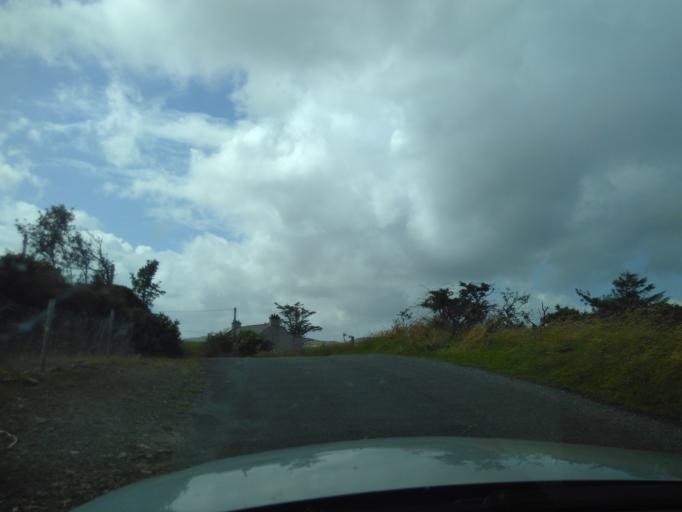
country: IE
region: Ulster
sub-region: County Donegal
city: Ramelton
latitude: 55.2228
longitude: -7.6218
